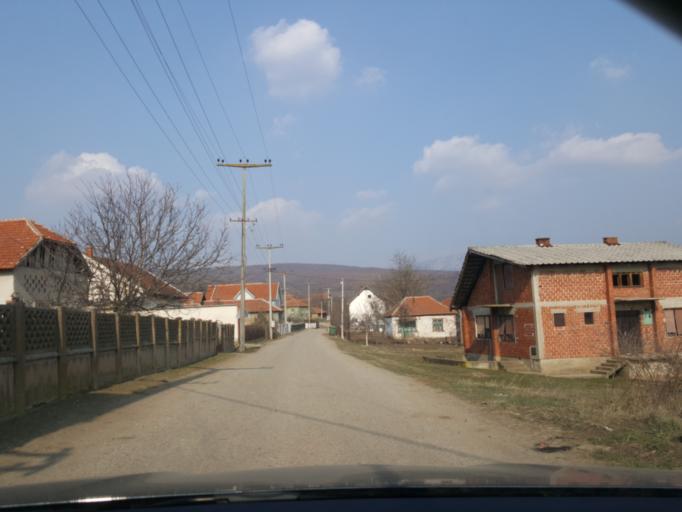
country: RS
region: Central Serbia
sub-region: Nisavski Okrug
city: Aleksinac
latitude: 43.5300
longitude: 21.7385
